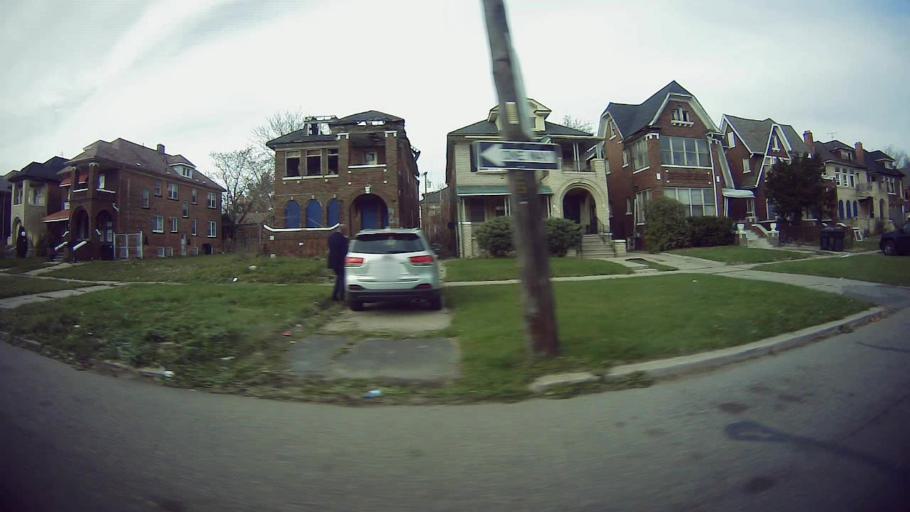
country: US
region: Michigan
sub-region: Wayne County
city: Highland Park
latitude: 42.3820
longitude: -83.1229
